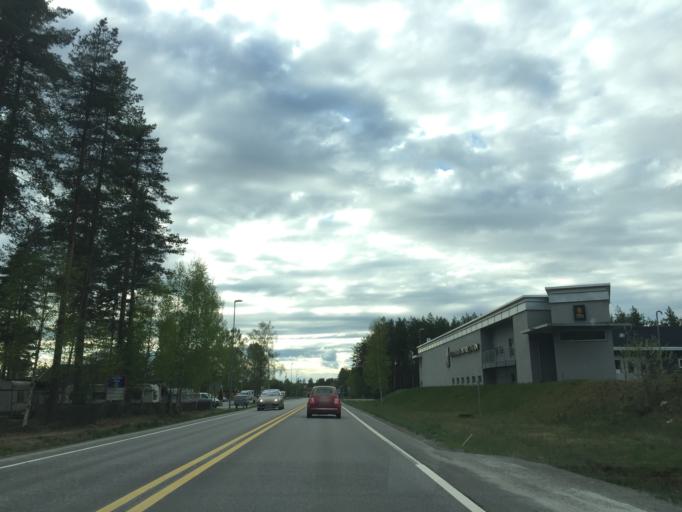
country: SE
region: Vaermland
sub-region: Eda Kommun
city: Charlottenberg
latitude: 59.9329
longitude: 12.2330
